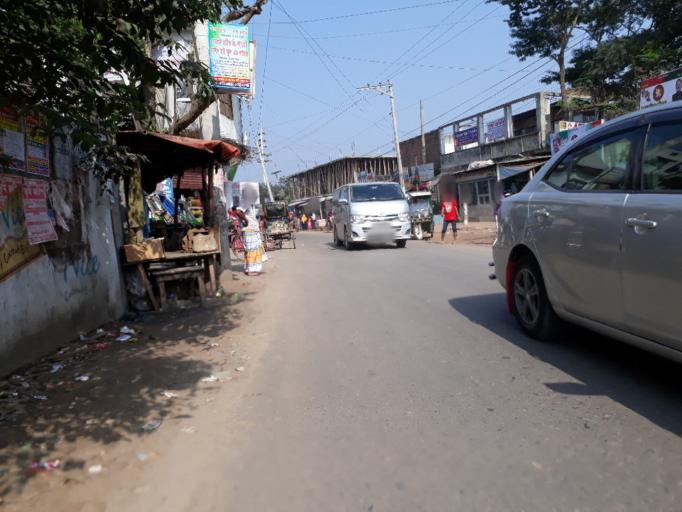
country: BD
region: Dhaka
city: Tungi
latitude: 23.8744
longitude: 90.3109
